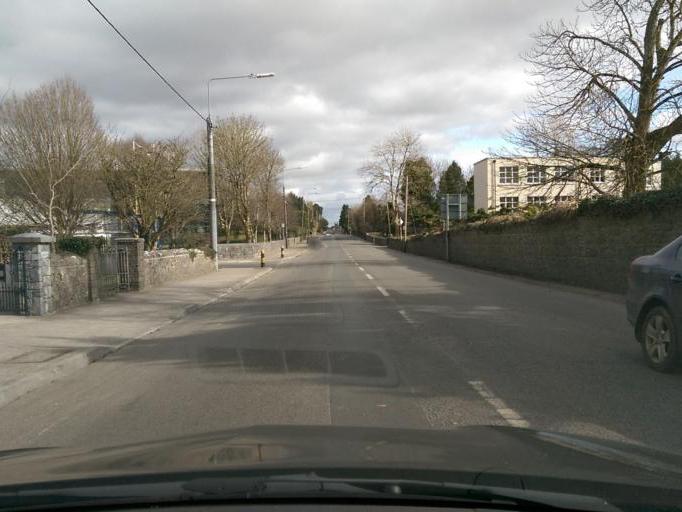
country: IE
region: Connaught
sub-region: County Galway
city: Ballinasloe
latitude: 53.3331
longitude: -8.2357
